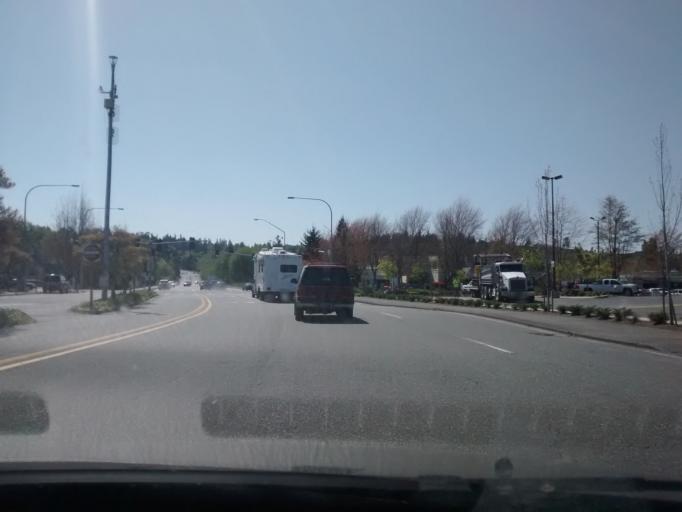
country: US
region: Washington
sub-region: Snohomish County
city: Edmonds
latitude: 47.8105
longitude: -122.3832
